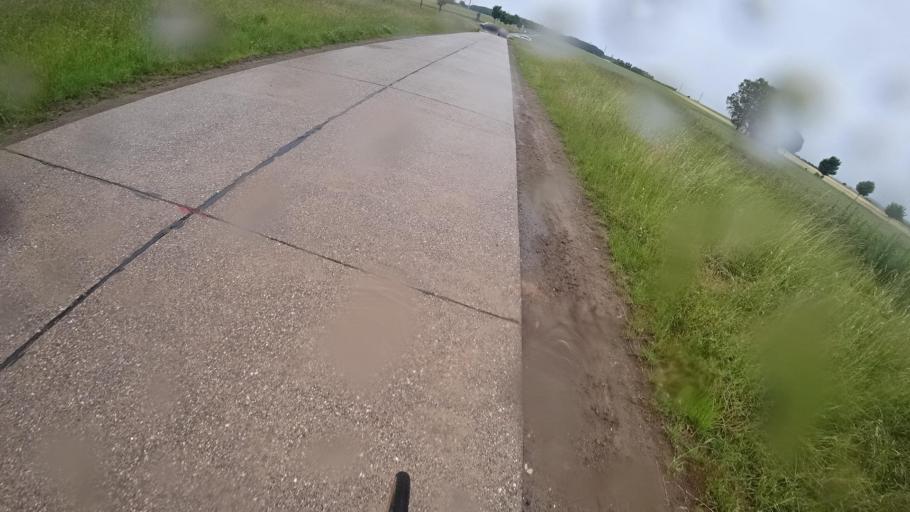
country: DE
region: Rheinland-Pfalz
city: Dernau
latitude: 50.5531
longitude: 7.0417
